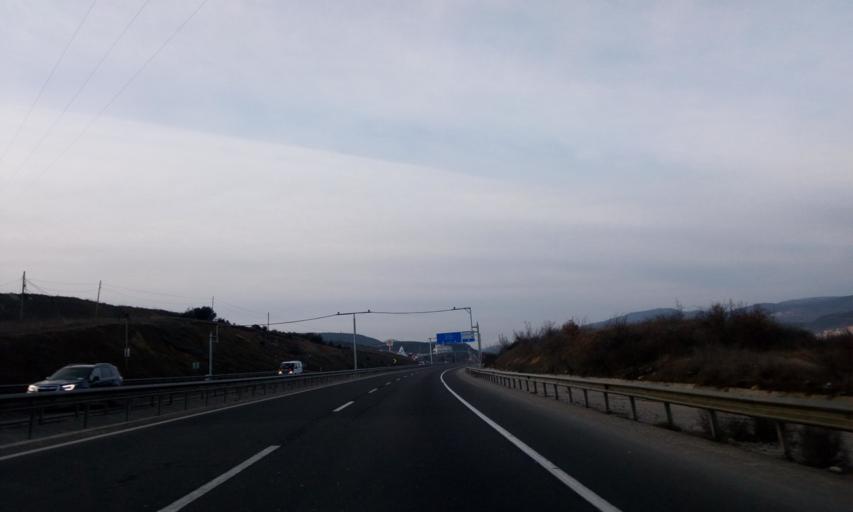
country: TR
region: Bilecik
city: Bilecik
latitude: 40.1393
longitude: 30.0251
